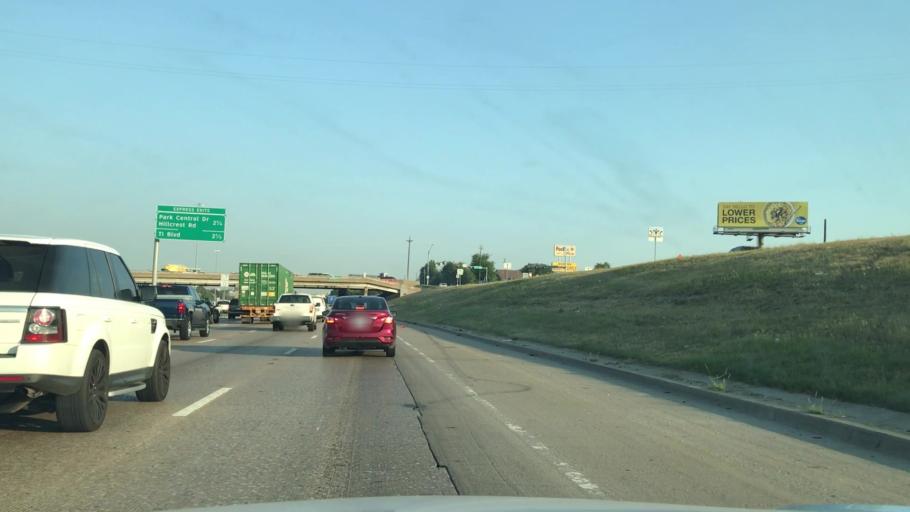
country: US
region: Texas
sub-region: Dallas County
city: Richardson
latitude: 32.8995
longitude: -96.7159
